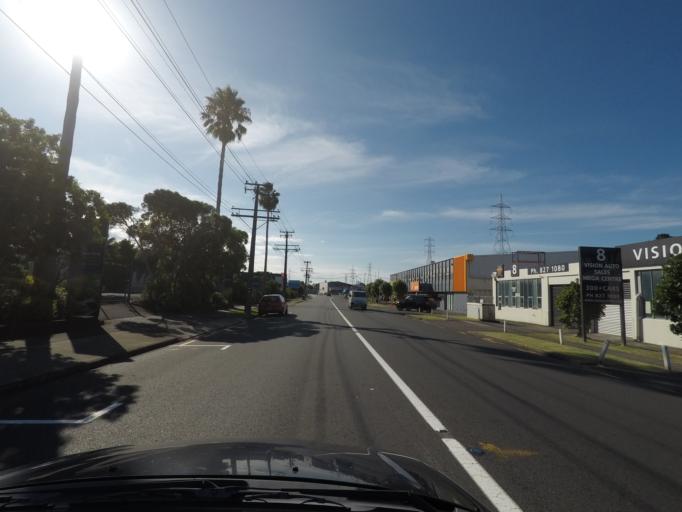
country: NZ
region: Auckland
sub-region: Auckland
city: Waitakere
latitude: -36.9049
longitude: 174.6899
